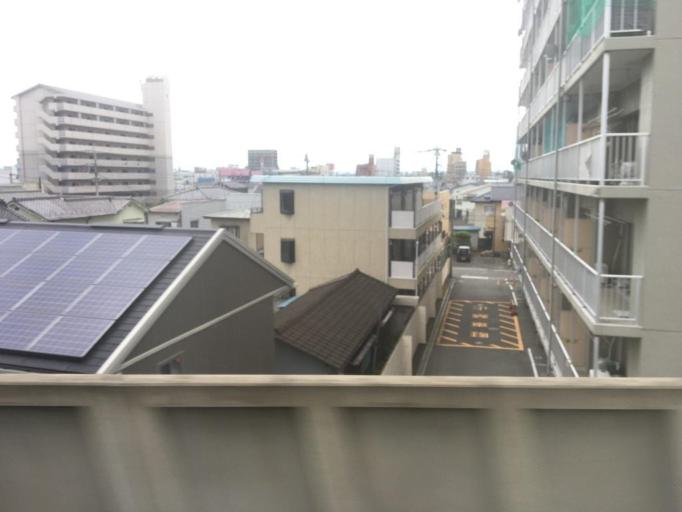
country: JP
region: Gunma
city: Isesaki
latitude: 36.3222
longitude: 139.2005
